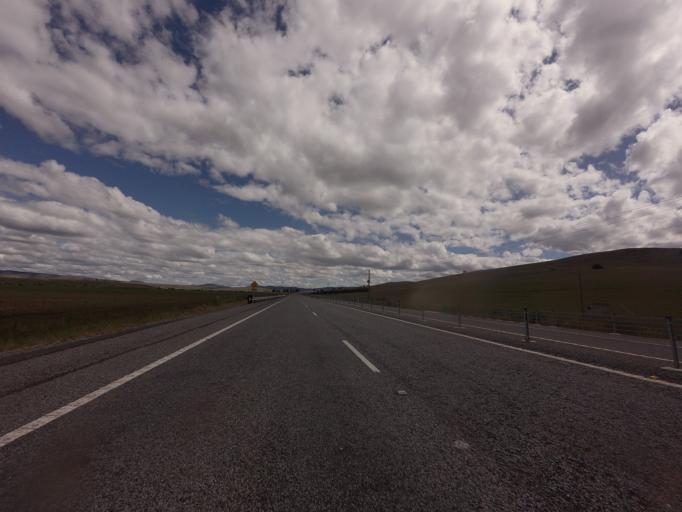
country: AU
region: Tasmania
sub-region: Northern Midlands
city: Evandale
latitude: -42.1049
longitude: 147.4487
